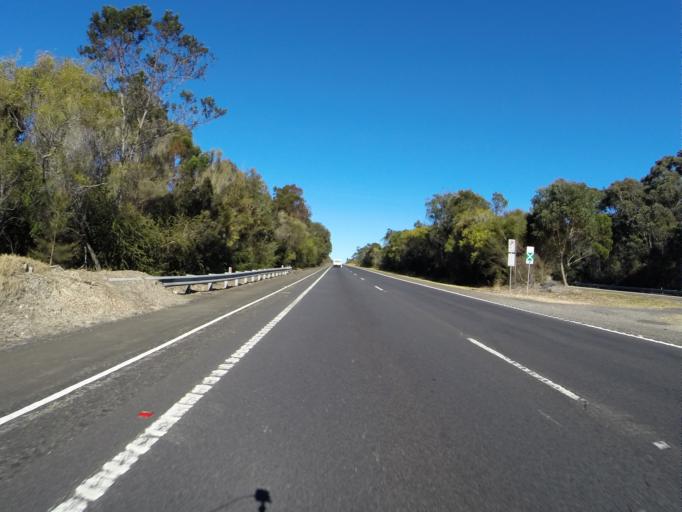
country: AU
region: New South Wales
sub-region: Wollongong
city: Helensburgh
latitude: -34.2170
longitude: 150.9562
